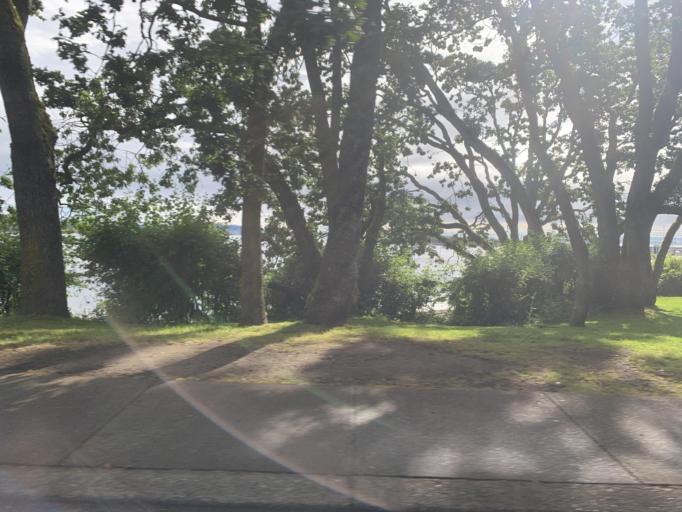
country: CA
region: British Columbia
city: Oak Bay
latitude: 48.4266
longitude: -123.3077
